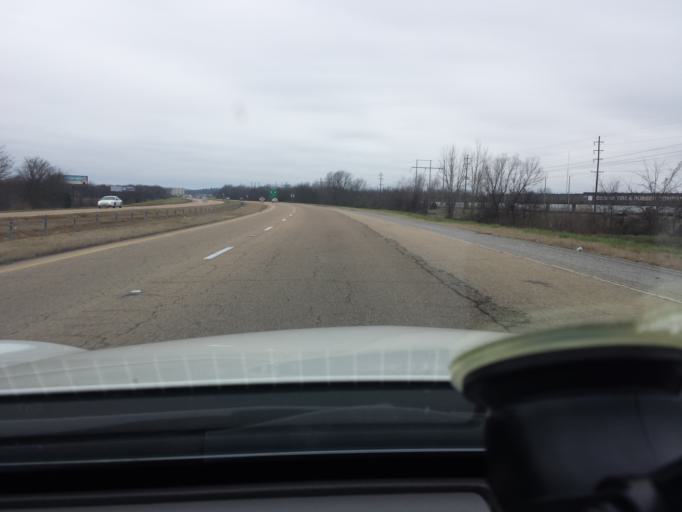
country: US
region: Mississippi
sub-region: Lee County
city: Tupelo
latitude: 34.2312
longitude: -88.7030
